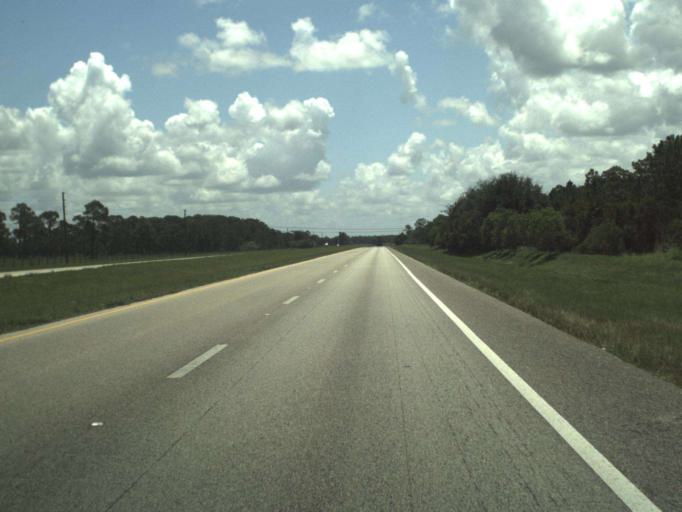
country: US
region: Florida
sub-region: Indian River County
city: Fellsmere
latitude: 27.6814
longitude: -80.8474
